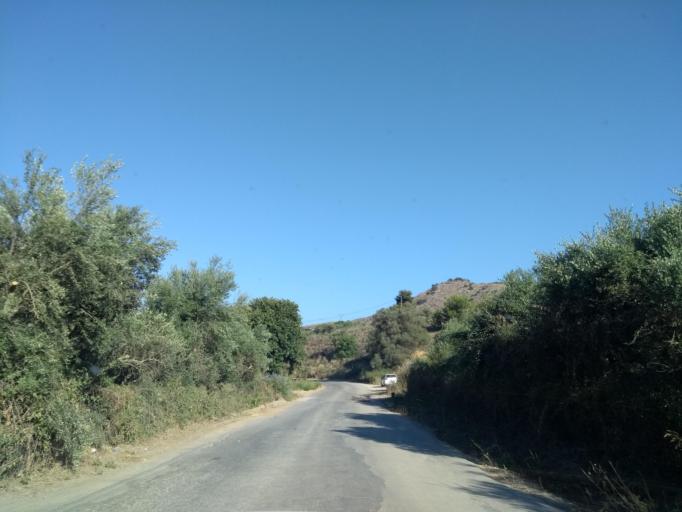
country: GR
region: Crete
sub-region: Nomos Chanias
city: Georgioupolis
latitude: 35.3659
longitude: 24.2358
